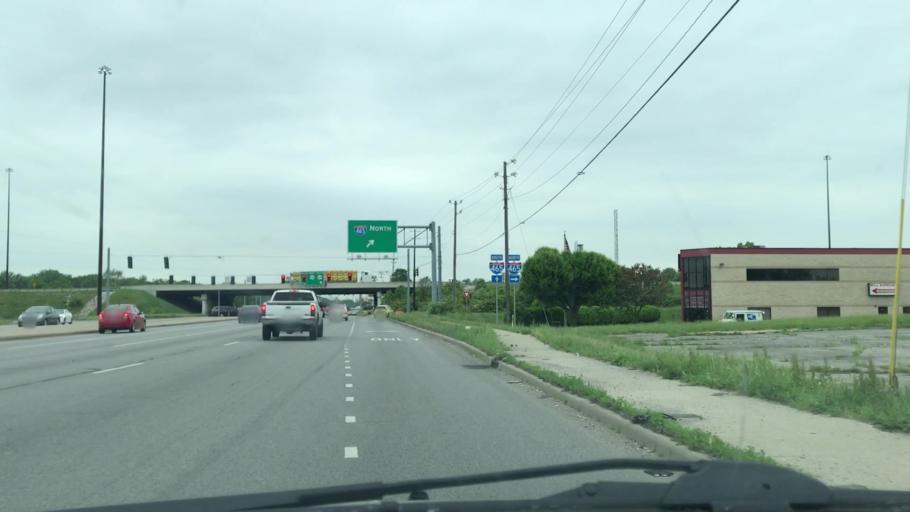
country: US
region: Indiana
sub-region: Marion County
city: Lawrence
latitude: 39.8334
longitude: -86.0337
